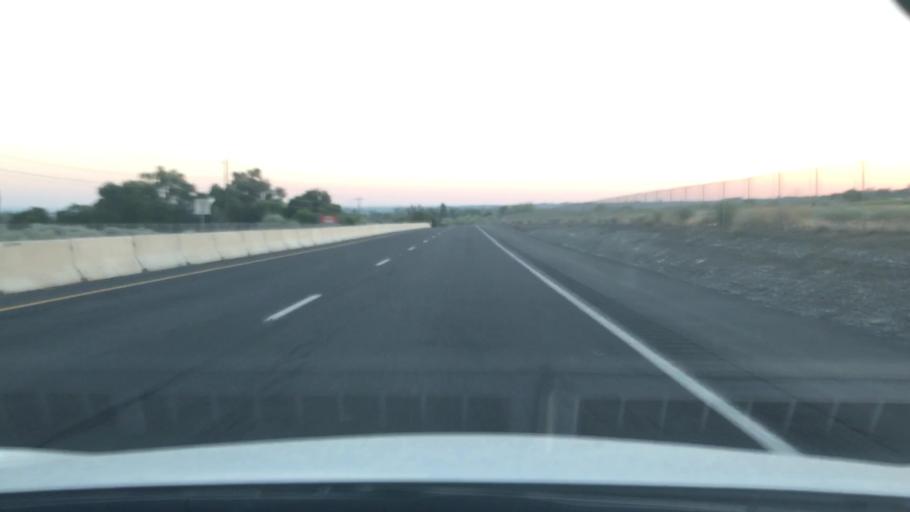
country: US
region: Washington
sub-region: Grant County
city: Moses Lake
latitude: 47.1331
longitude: -119.2567
